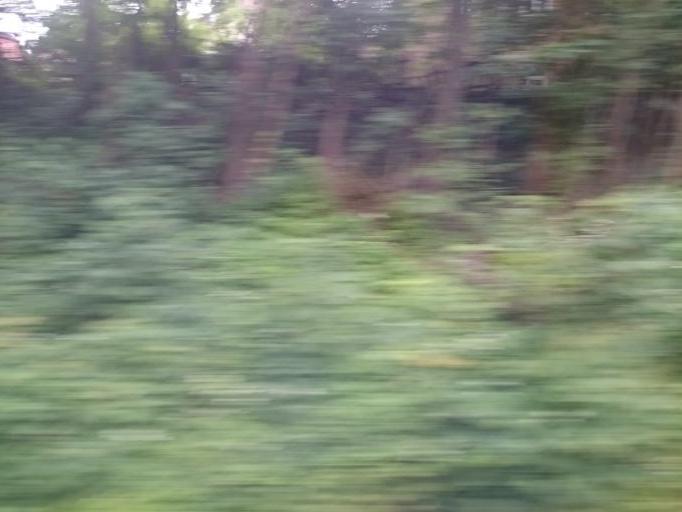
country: DE
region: Bavaria
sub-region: Upper Bavaria
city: Munich
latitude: 48.1201
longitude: 11.5830
